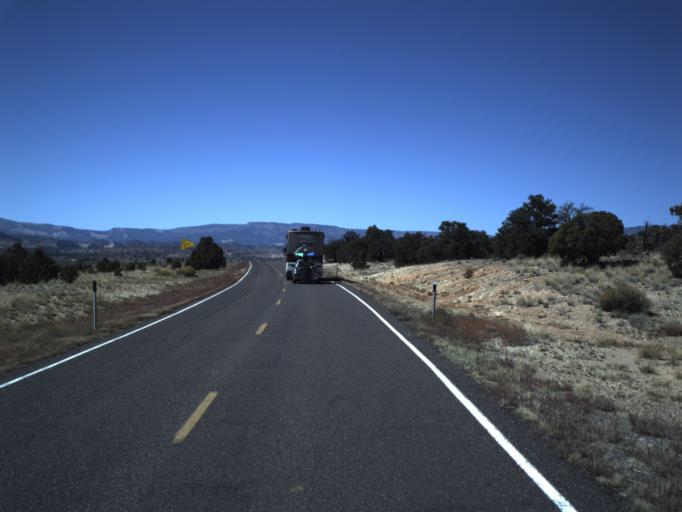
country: US
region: Utah
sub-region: Wayne County
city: Loa
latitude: 37.7375
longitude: -111.5467
